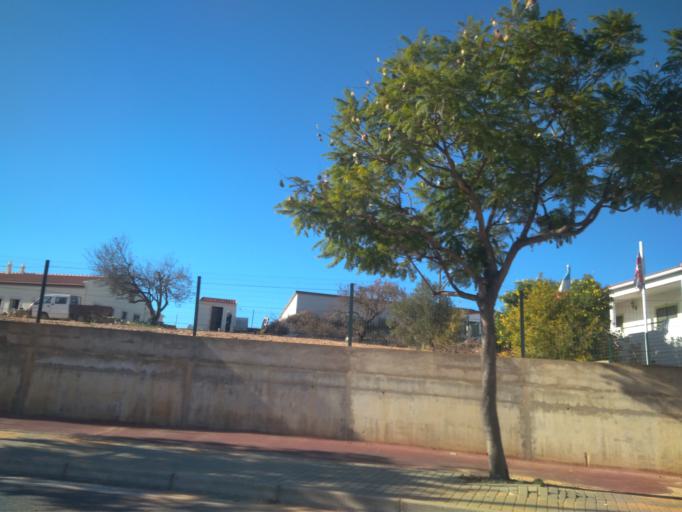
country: PT
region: Faro
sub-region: Albufeira
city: Ferreiras
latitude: 37.1168
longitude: -8.2286
